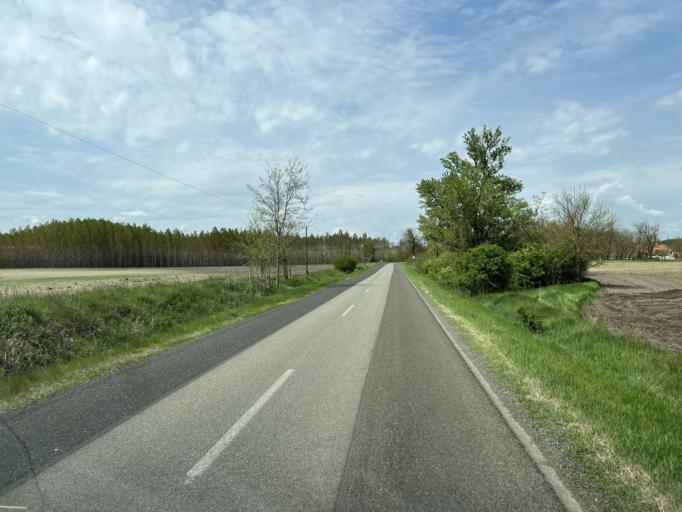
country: HU
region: Pest
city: Albertirsa
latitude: 47.1662
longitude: 19.6158
